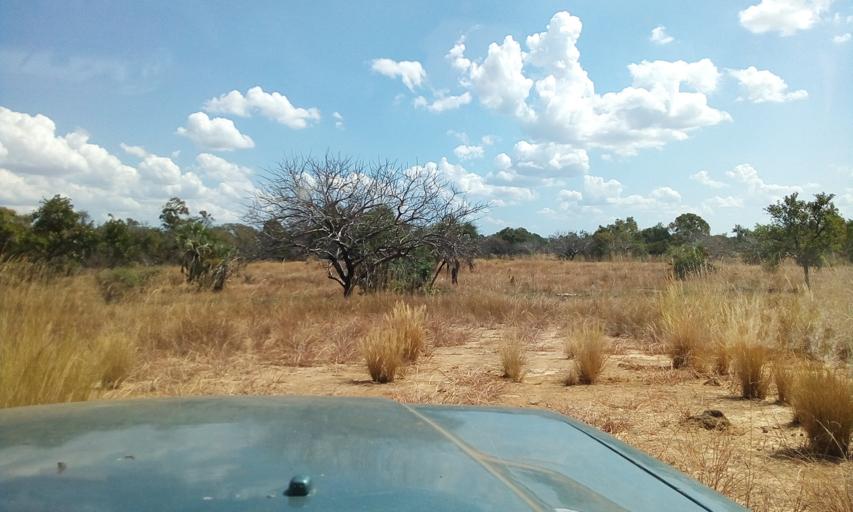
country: MG
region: Melaky
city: Mahabe
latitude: -16.4373
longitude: 45.3731
